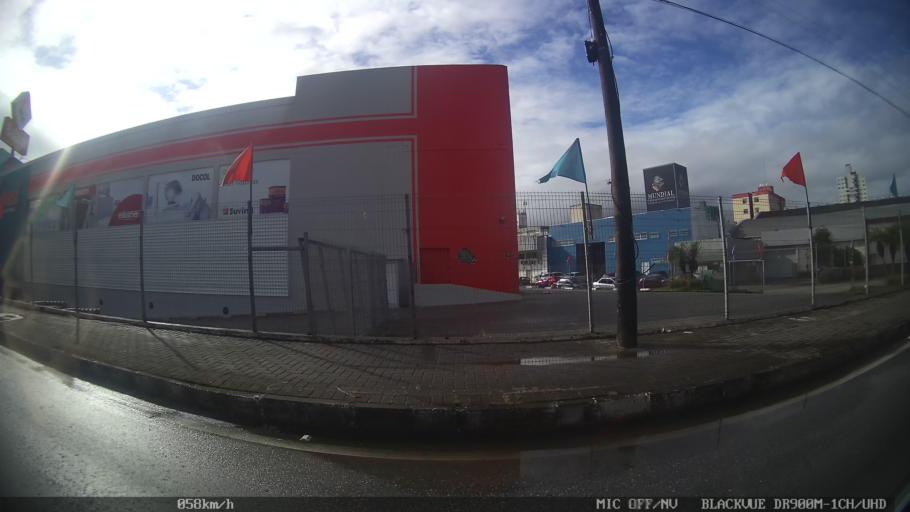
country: BR
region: Santa Catarina
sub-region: Sao Jose
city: Campinas
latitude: -27.5671
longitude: -48.6138
